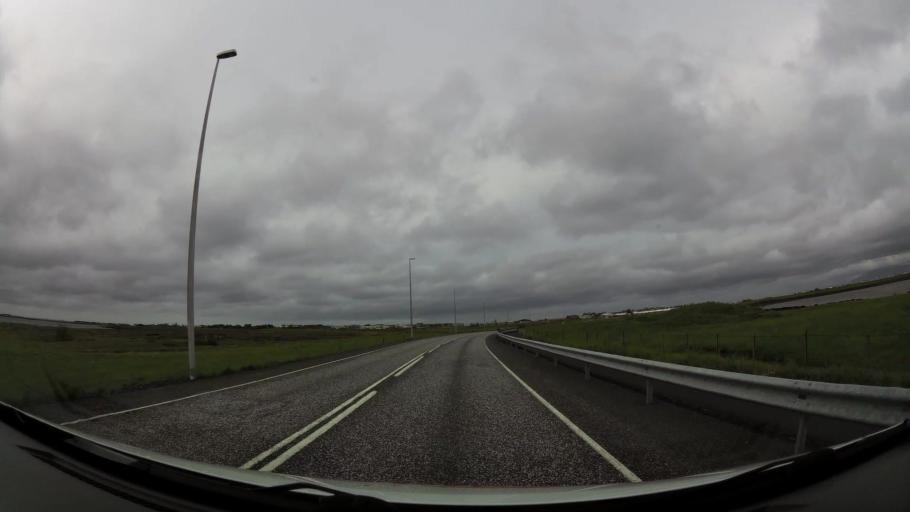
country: IS
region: Capital Region
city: Alftanes
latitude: 64.0971
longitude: -22.0030
